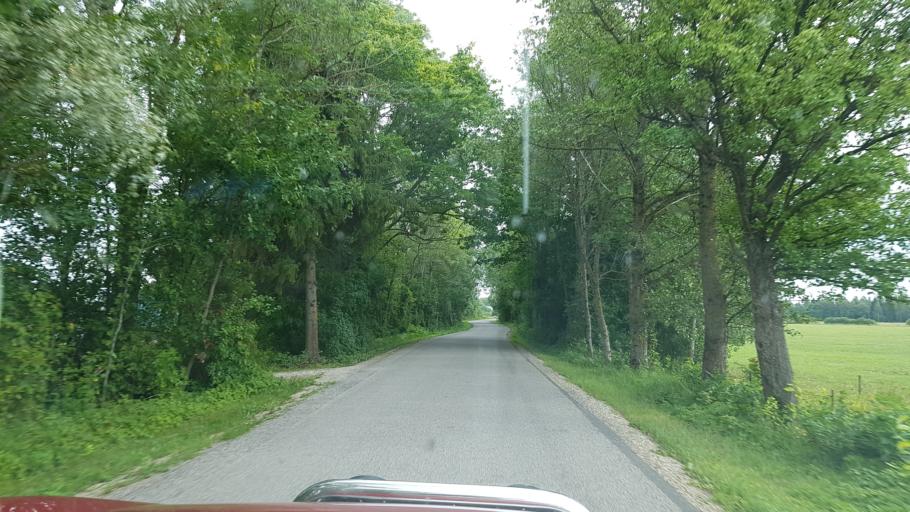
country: EE
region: Laeaene
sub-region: Ridala Parish
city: Uuemoisa
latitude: 58.9758
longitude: 23.7699
